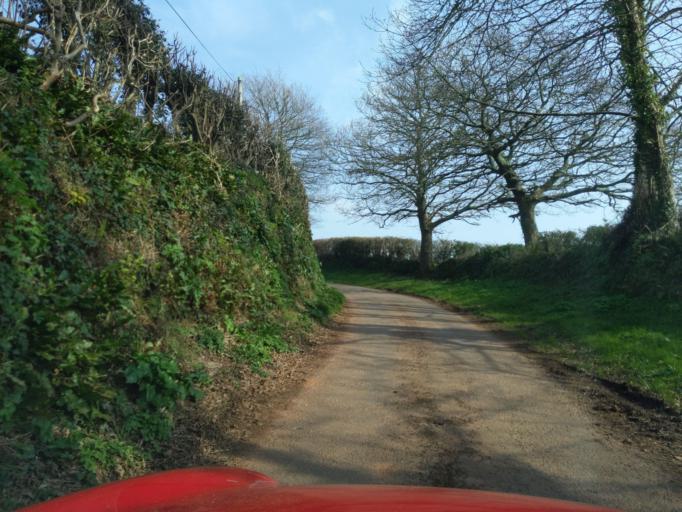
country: GB
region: England
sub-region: Devon
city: Kingsbridge
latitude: 50.2855
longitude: -3.7233
